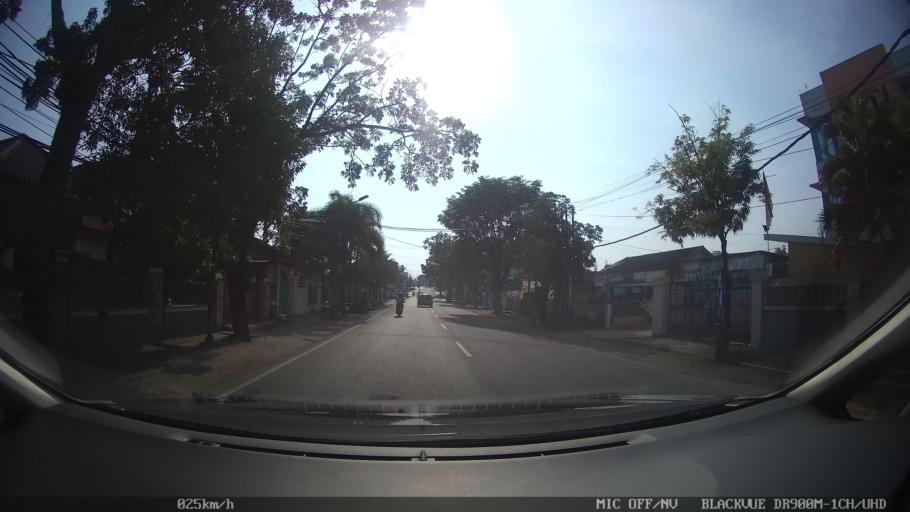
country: ID
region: Lampung
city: Bandarlampung
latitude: -5.4189
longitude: 105.2475
